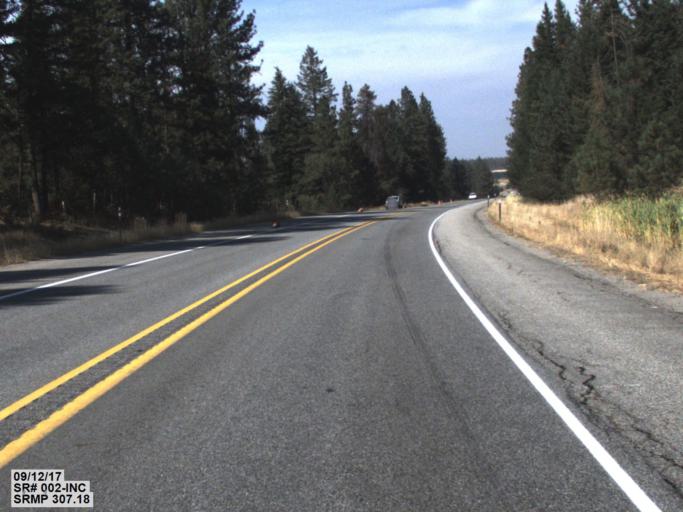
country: US
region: Washington
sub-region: Spokane County
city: Deer Park
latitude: 47.9282
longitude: -117.3514
